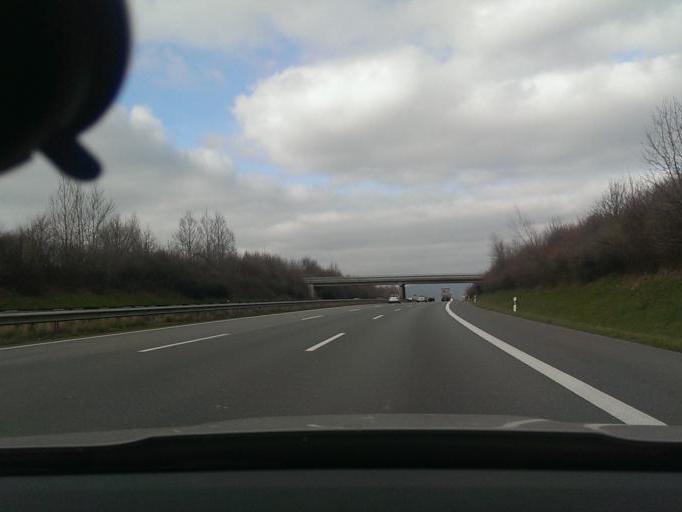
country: DE
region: North Rhine-Westphalia
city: Bad Oeynhausen
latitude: 52.1721
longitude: 8.8160
